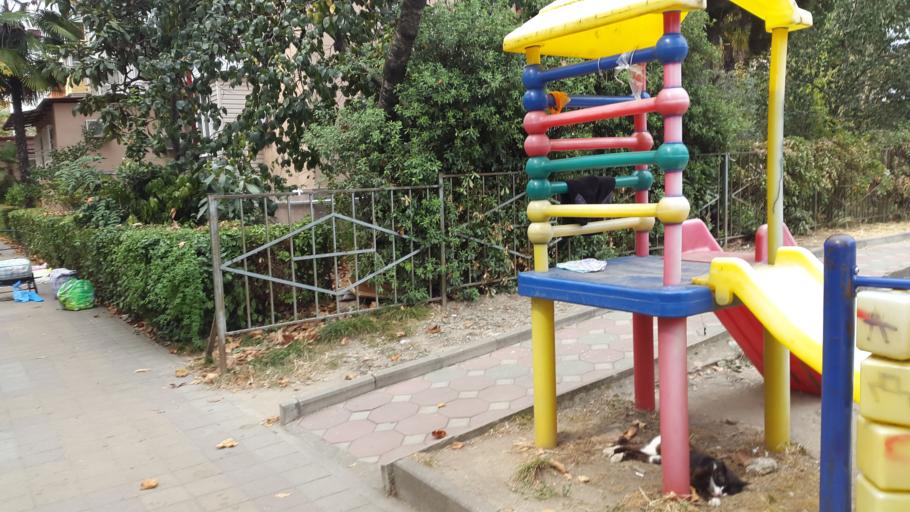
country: RU
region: Krasnodarskiy
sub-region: Sochi City
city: Sochi
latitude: 43.6007
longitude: 39.7287
